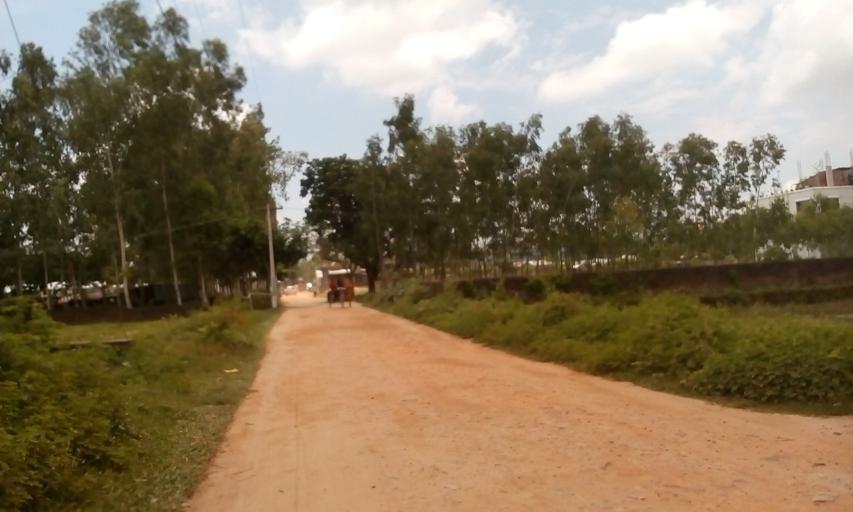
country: IN
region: West Bengal
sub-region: Dakshin Dinajpur
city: Balurghat
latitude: 25.3853
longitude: 88.9904
